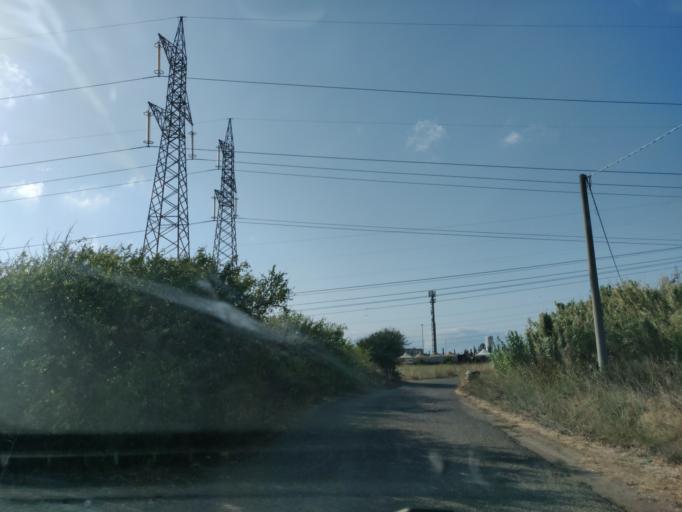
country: IT
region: Latium
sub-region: Citta metropolitana di Roma Capitale
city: Aurelia
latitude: 42.1280
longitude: 11.7680
